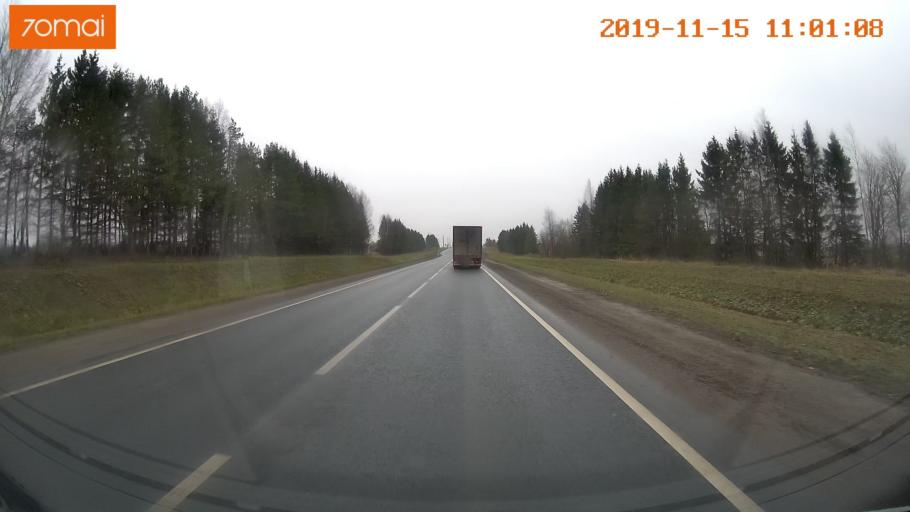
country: RU
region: Vologda
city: Chebsara
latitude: 59.1342
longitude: 38.9141
